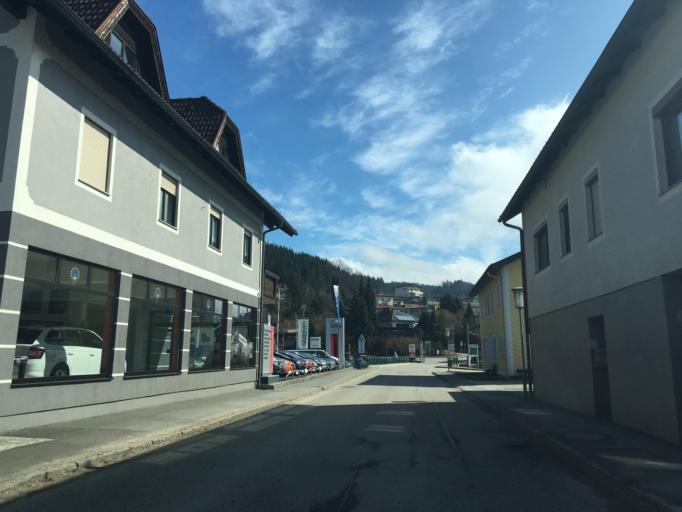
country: AT
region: Lower Austria
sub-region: Politischer Bezirk Melk
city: Nochling
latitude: 48.2722
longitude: 14.9509
